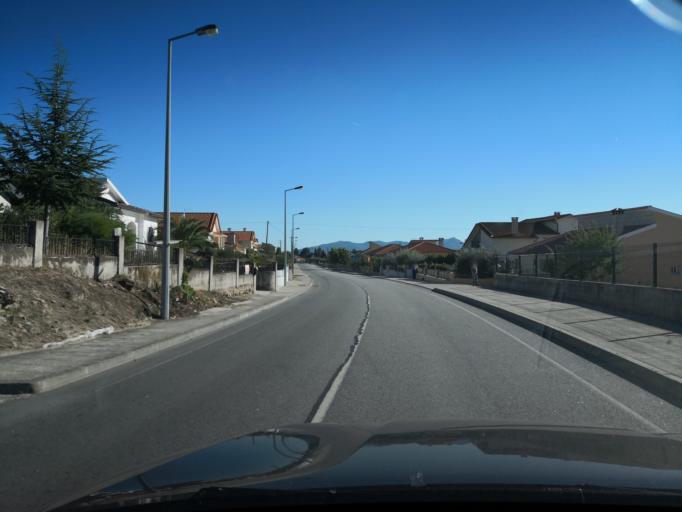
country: PT
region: Vila Real
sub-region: Valpacos
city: Valpacos
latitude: 41.6272
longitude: -7.3129
